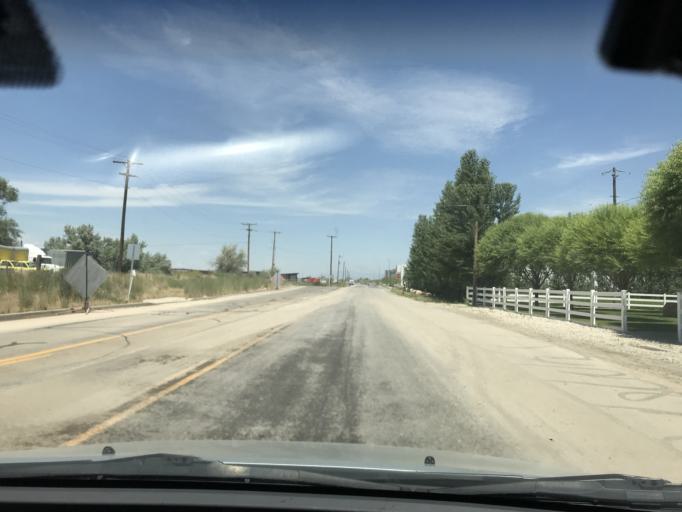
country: US
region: Utah
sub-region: Davis County
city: North Salt Lake
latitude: 40.8121
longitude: -111.9536
